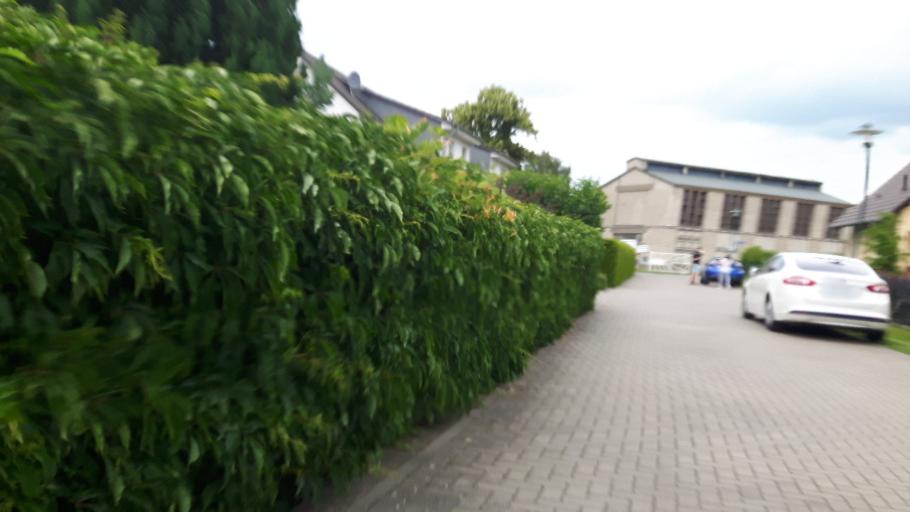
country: DE
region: Brandenburg
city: Schwedt (Oder)
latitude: 53.0491
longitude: 14.2760
